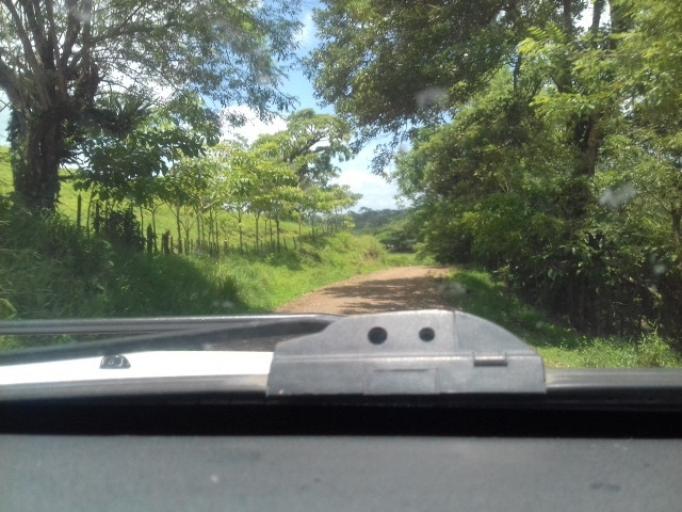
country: NI
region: Matagalpa
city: Matiguas
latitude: 13.0164
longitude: -85.4028
